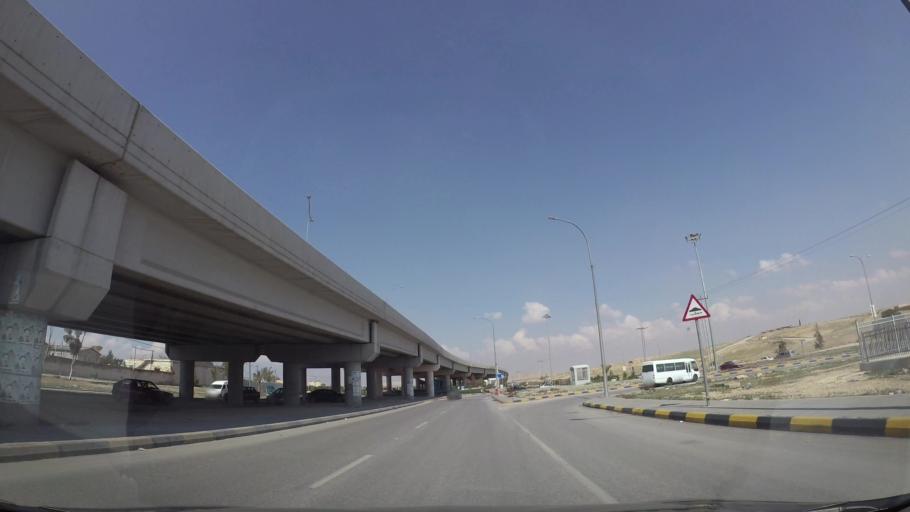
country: JO
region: Zarqa
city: Zarqa
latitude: 32.0806
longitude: 36.1062
